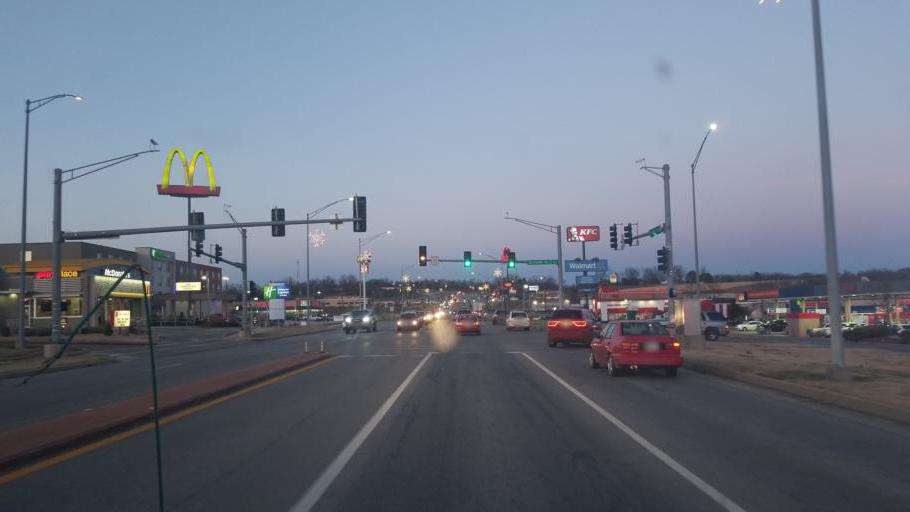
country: US
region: Missouri
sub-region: Howell County
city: West Plains
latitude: 36.7138
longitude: -91.8746
